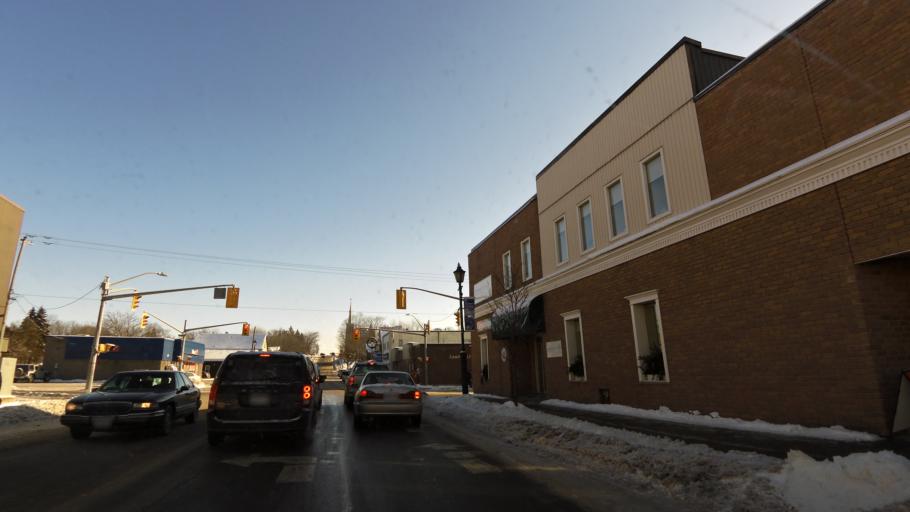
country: CA
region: Ontario
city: Quinte West
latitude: 44.3081
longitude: -77.7969
